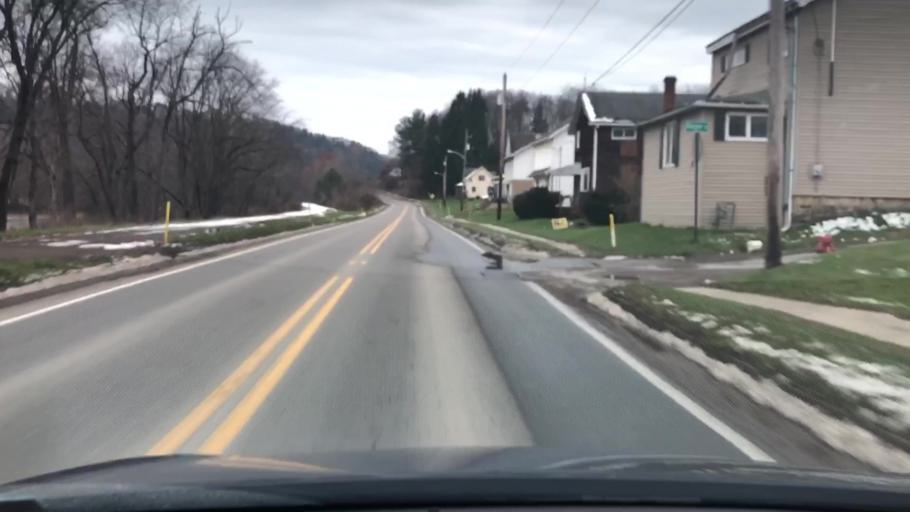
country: US
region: Pennsylvania
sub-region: Clarion County
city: Clarion
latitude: 41.0173
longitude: -79.2762
